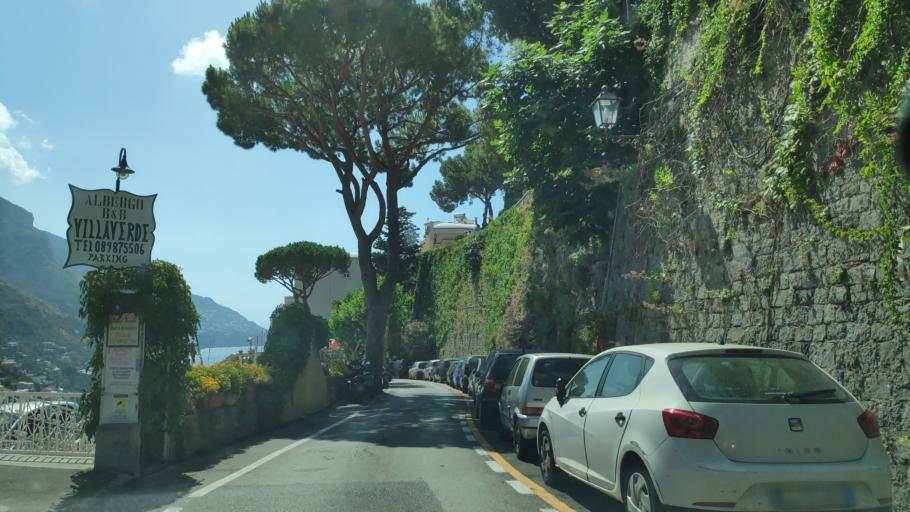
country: IT
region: Campania
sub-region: Provincia di Salerno
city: Positano
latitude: 40.6295
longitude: 14.4827
